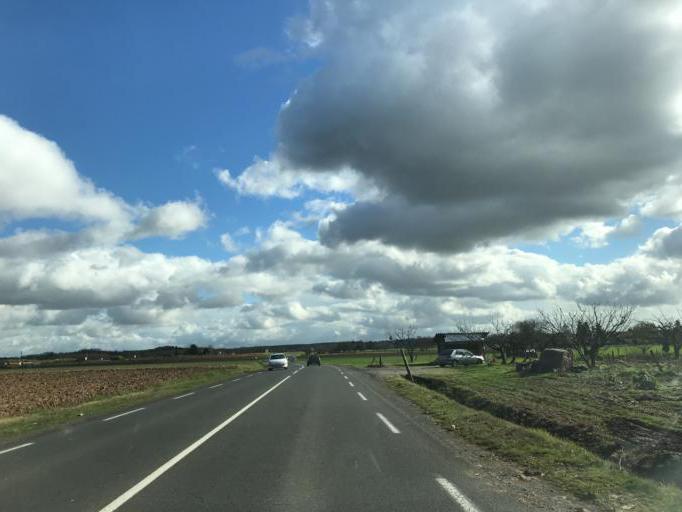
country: FR
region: Rhone-Alpes
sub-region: Departement de l'Ain
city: Frans
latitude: 45.9865
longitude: 4.7867
